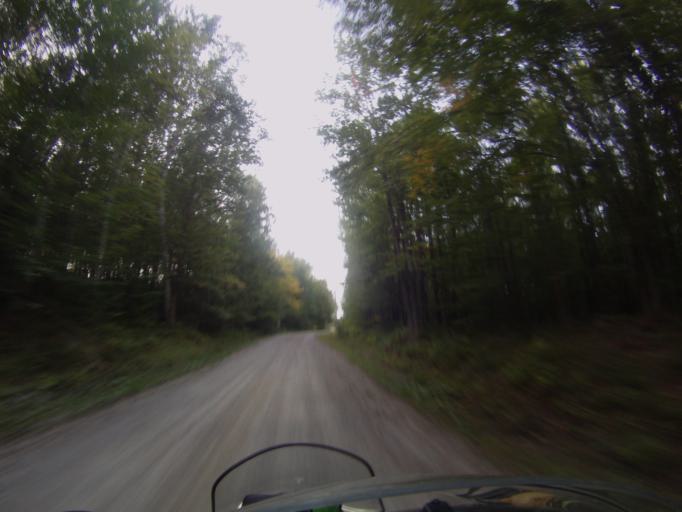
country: US
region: Vermont
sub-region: Addison County
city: Middlebury (village)
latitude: 43.9957
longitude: -73.0442
